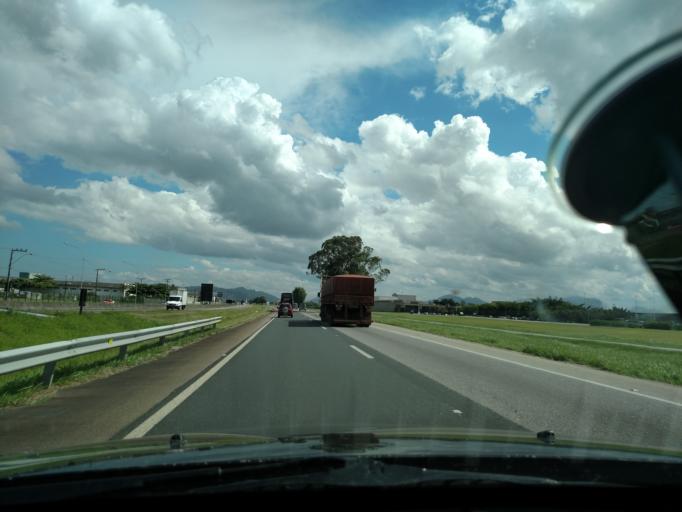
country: BR
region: Santa Catarina
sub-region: Tijucas
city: Tijucas
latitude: -27.2193
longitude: -48.6256
